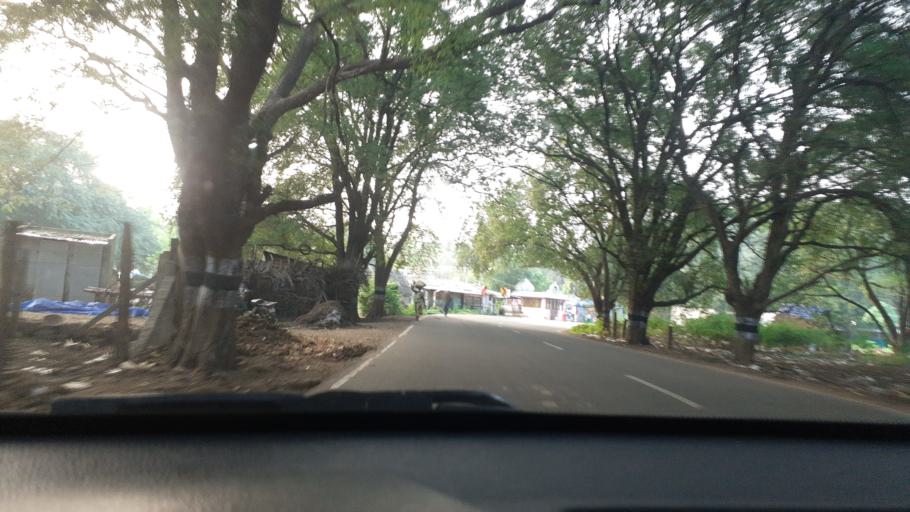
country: IN
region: Tamil Nadu
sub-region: Dindigul
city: Ayakudi
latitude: 10.4104
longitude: 77.5388
